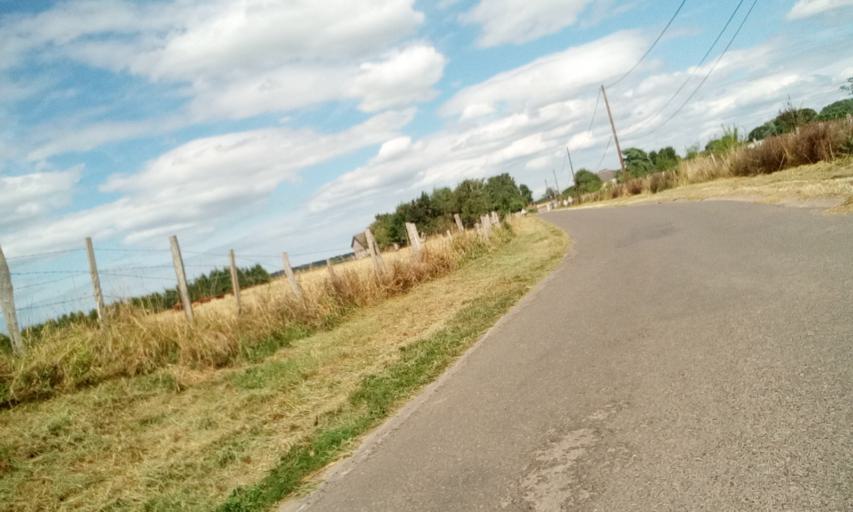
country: FR
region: Lower Normandy
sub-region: Departement du Calvados
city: Sannerville
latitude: 49.1621
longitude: -0.2155
